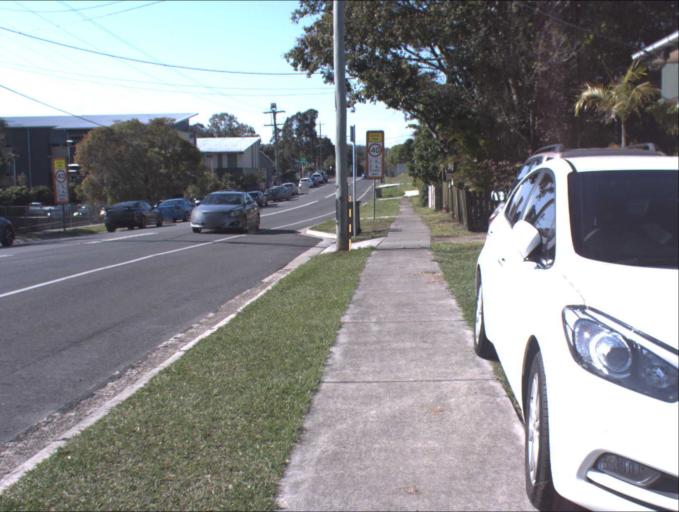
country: AU
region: Queensland
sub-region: Logan
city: Waterford West
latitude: -27.6953
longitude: 153.1431
